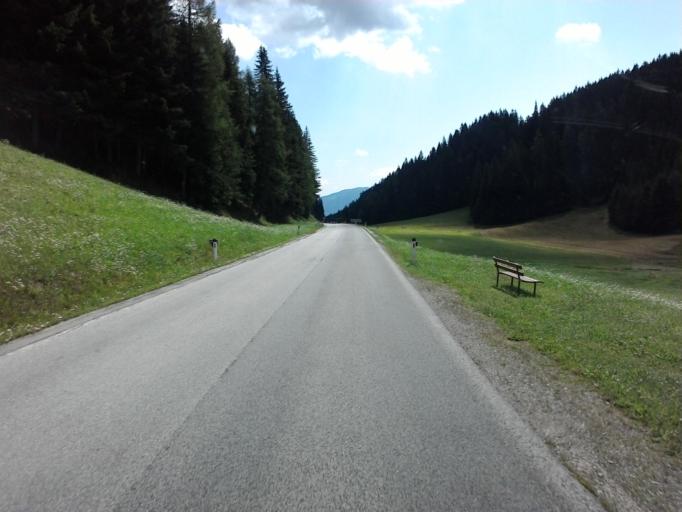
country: AT
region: Tyrol
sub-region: Politischer Bezirk Lienz
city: Kartitsch
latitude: 46.7186
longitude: 12.5371
